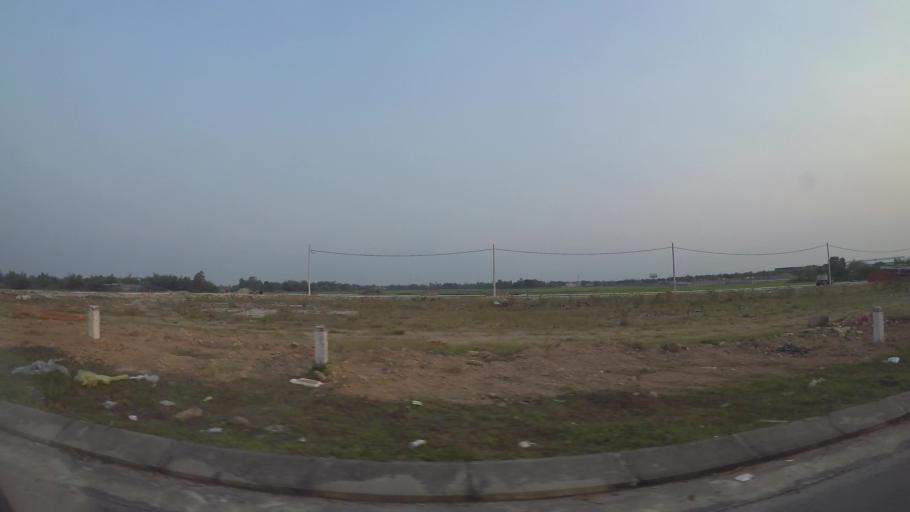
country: VN
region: Da Nang
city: Cam Le
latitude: 15.9677
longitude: 108.2142
